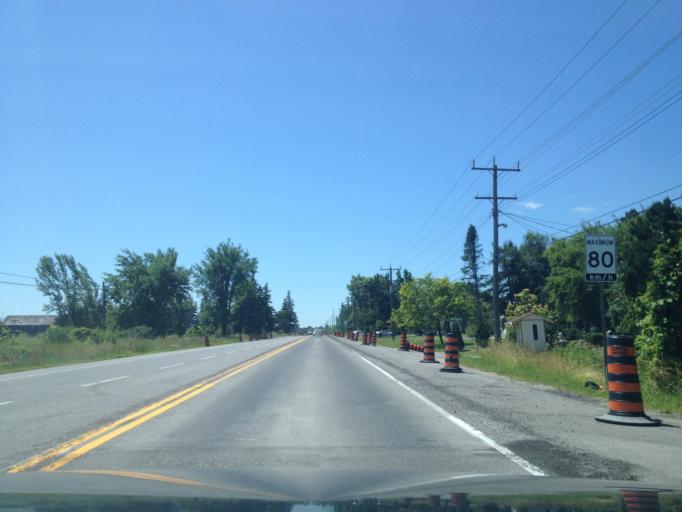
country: CA
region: Ontario
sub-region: Halton
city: Milton
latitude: 43.6463
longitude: -80.0185
